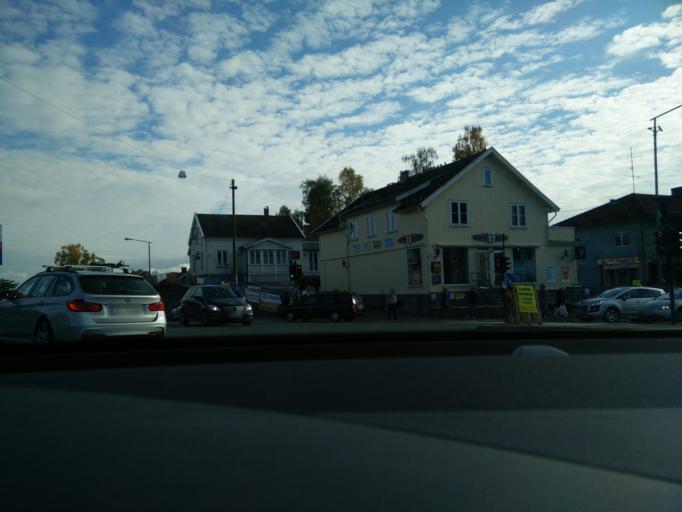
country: NO
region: Akershus
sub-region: Baerum
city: Lysaker
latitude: 59.9477
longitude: 10.6429
